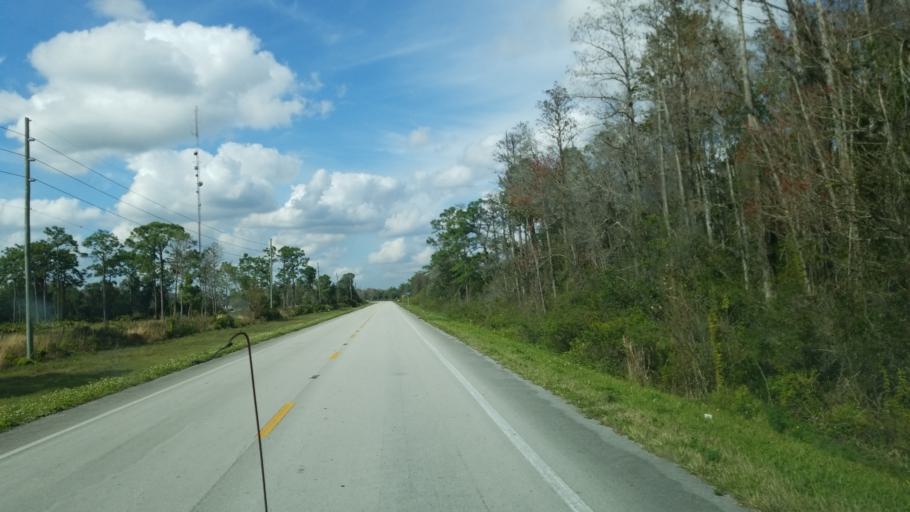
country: US
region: Florida
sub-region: Brevard County
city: June Park
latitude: 27.9959
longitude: -81.0185
